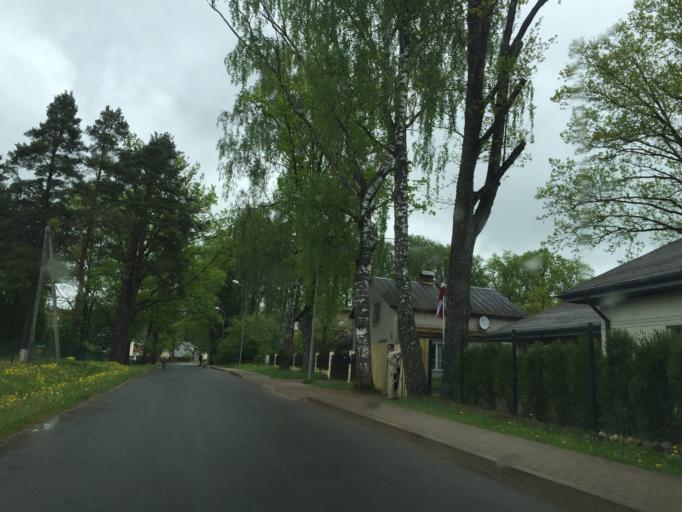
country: LV
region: Lielvarde
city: Lielvarde
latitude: 56.7253
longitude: 24.8050
